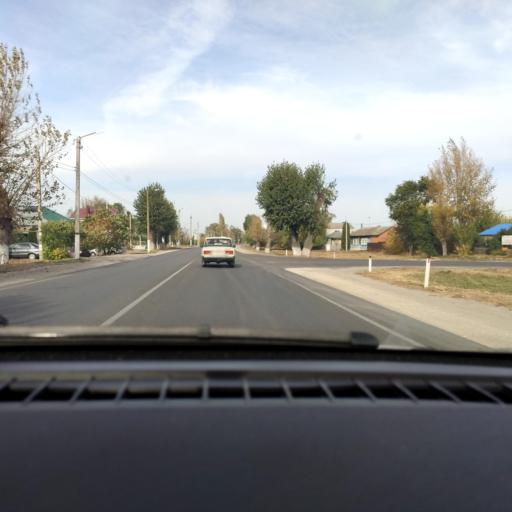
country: RU
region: Voronezj
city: Novaya Usman'
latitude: 51.6188
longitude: 39.3962
